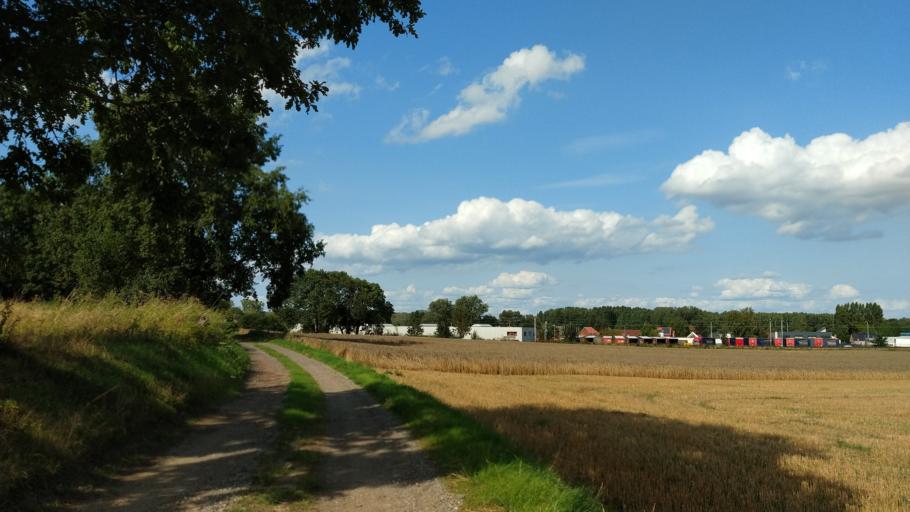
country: BE
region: Flanders
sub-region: Provincie Vlaams-Brabant
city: Boutersem
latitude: 50.8328
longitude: 4.8475
